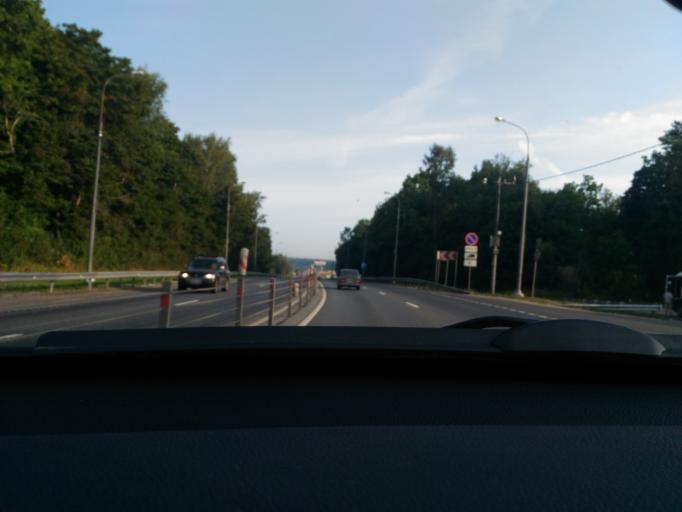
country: RU
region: Moskovskaya
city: Marfino
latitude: 56.0358
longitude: 37.5430
